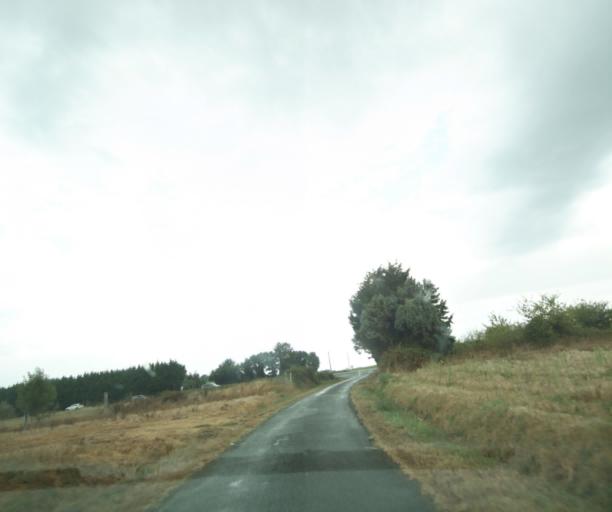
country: FR
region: Poitou-Charentes
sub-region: Departement de la Charente-Maritime
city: Cabariot
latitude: 45.9481
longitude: -0.8681
